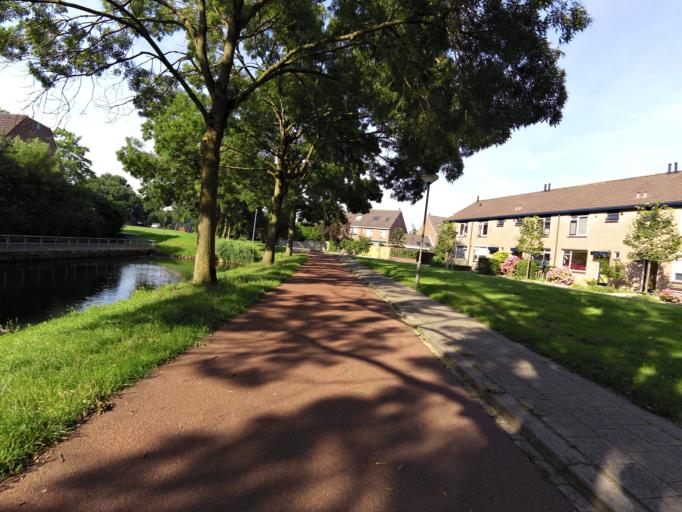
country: NL
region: South Holland
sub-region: Gemeente Papendrecht
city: Papendrecht
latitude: 51.7991
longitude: 4.7247
